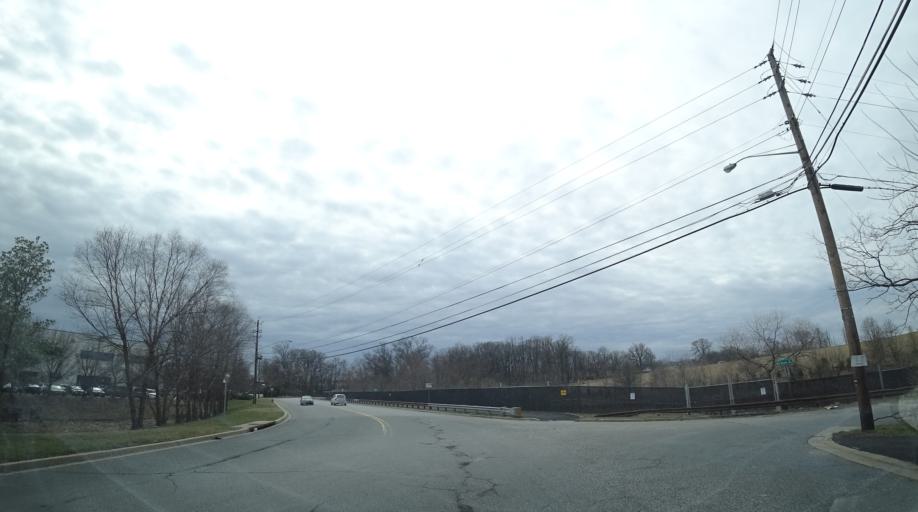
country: US
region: Maryland
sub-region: Montgomery County
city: Rockville
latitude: 39.0983
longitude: -77.1421
